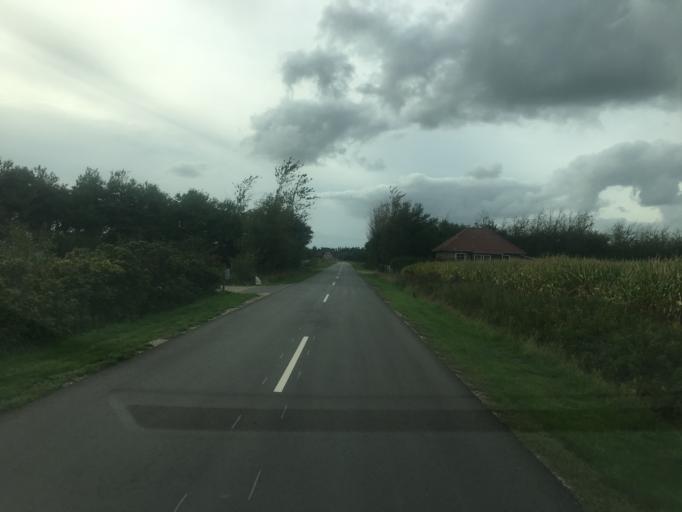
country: DE
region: Schleswig-Holstein
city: Aventoft
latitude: 54.9669
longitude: 8.7844
